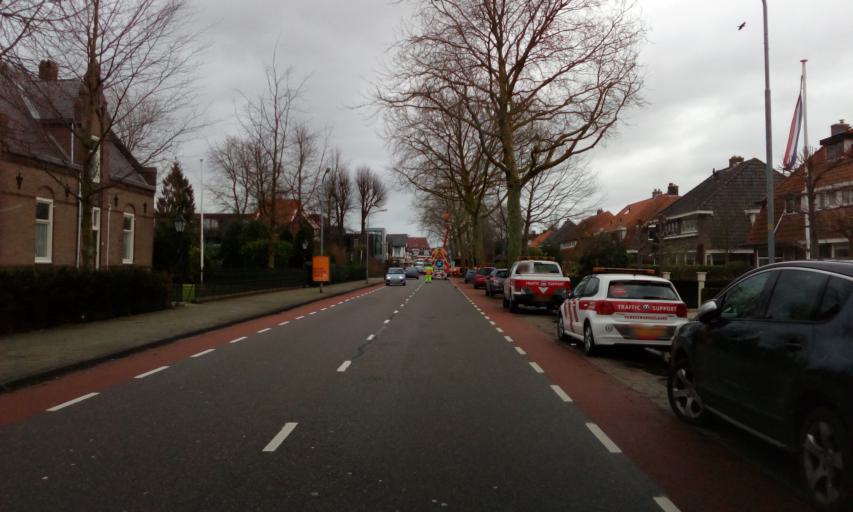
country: NL
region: North Holland
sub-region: Gemeente Wijdemeren
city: Kortenhoef
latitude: 52.2392
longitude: 5.1182
